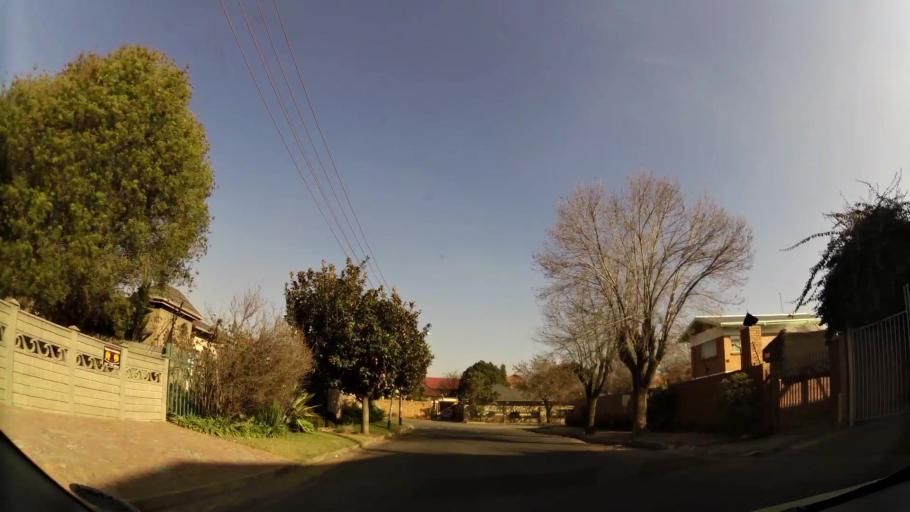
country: ZA
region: Gauteng
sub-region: West Rand District Municipality
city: Randfontein
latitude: -26.1773
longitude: 27.7057
